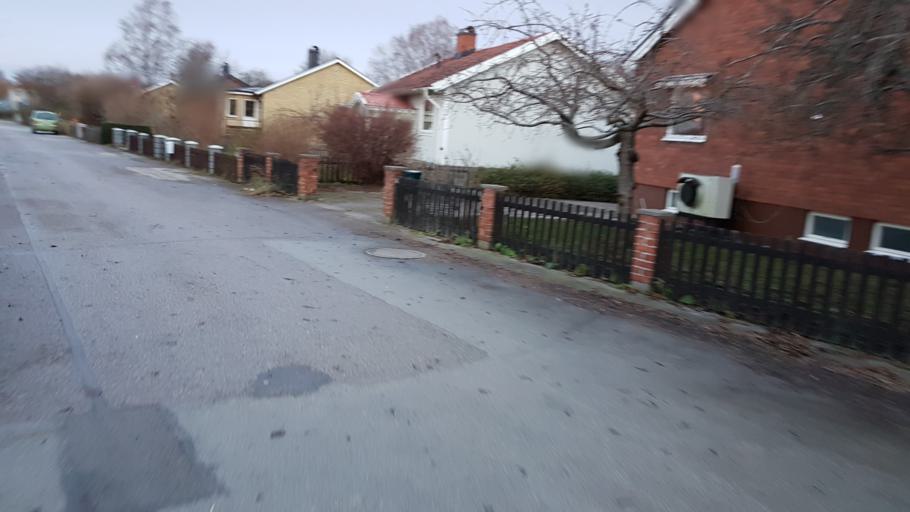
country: SE
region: Gotland
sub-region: Gotland
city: Visby
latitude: 57.6228
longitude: 18.2923
